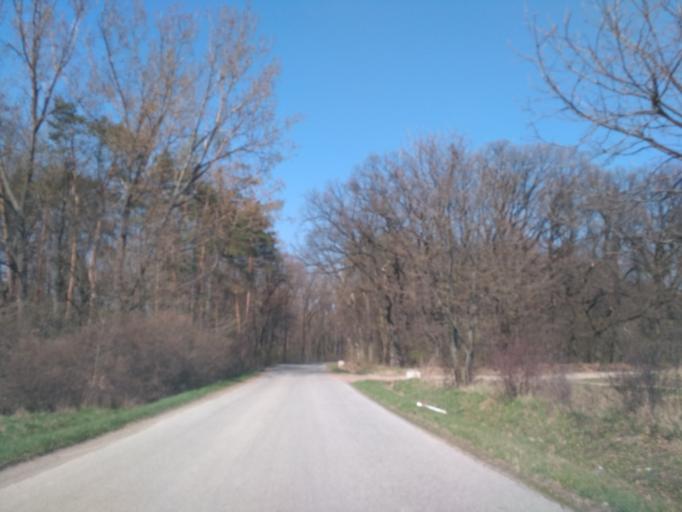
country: SK
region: Kosicky
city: Secovce
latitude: 48.7942
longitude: 21.6645
